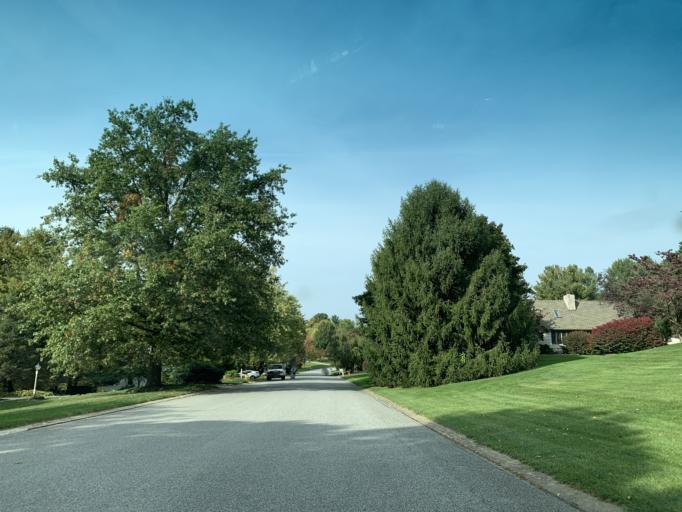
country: US
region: Pennsylvania
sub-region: York County
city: Spry
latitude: 39.9265
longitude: -76.6738
